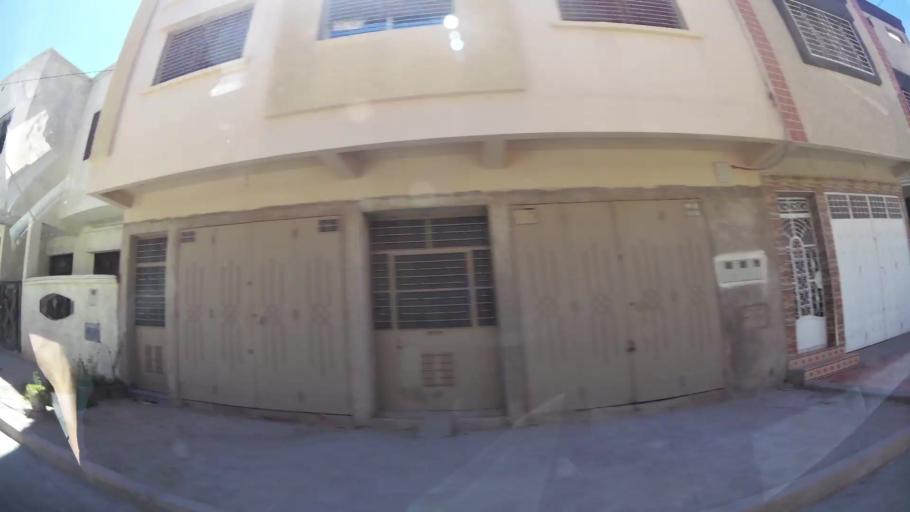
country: MA
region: Oriental
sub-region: Oujda-Angad
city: Oujda
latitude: 34.6853
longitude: -1.8685
